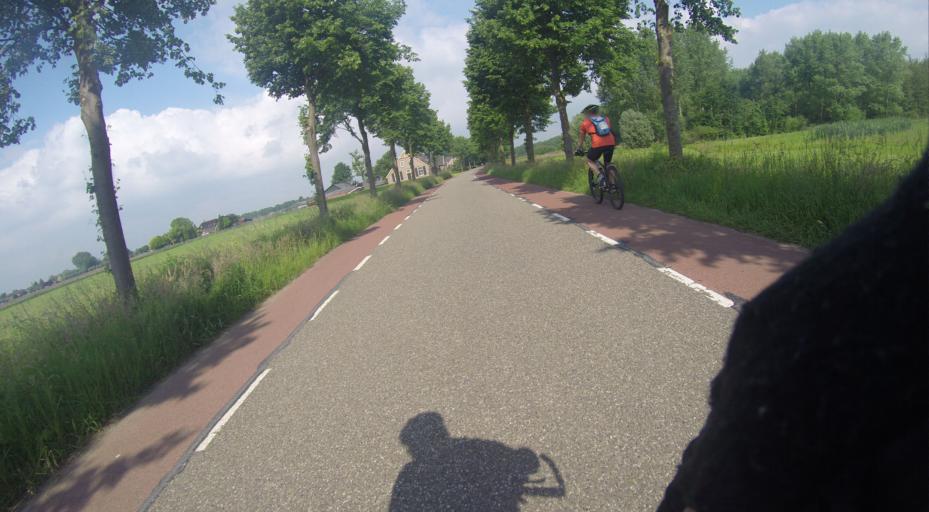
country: NL
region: Gelderland
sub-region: Gemeente Bronckhorst
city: Baak
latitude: 52.0721
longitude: 6.2103
